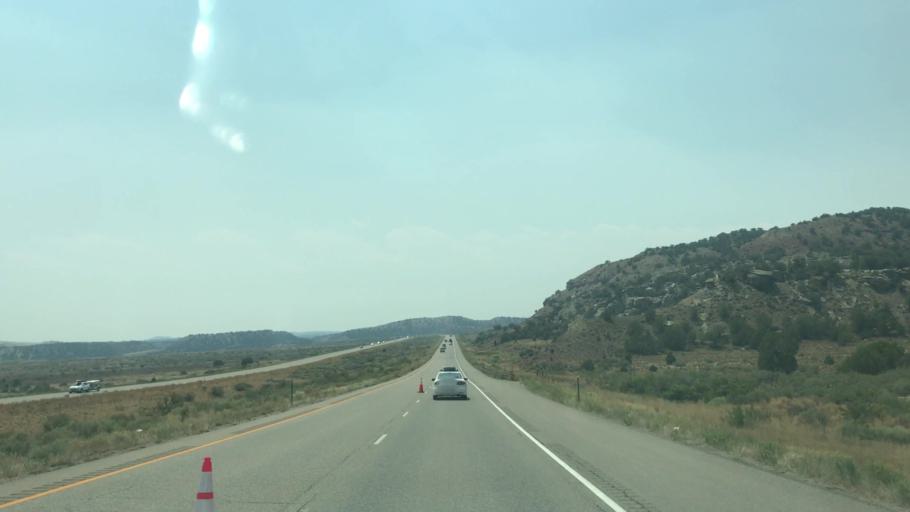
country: US
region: Colorado
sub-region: Garfield County
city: Parachute
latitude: 39.3897
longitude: -108.1354
